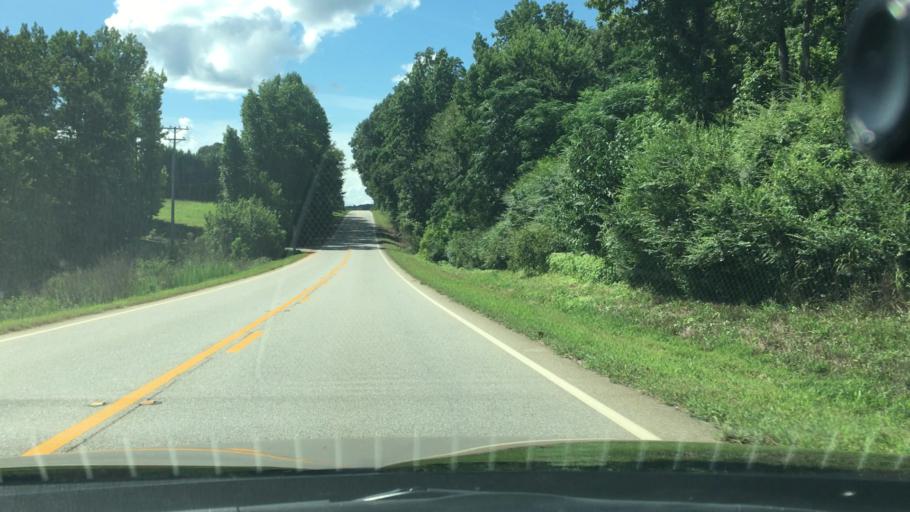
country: US
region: Georgia
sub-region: Jasper County
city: Monticello
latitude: 33.3093
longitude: -83.7415
